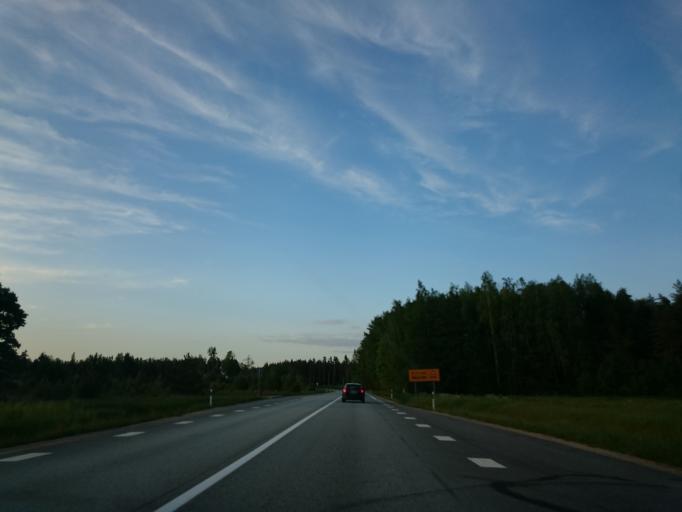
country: LV
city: Tireli
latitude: 56.8631
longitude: 23.6177
